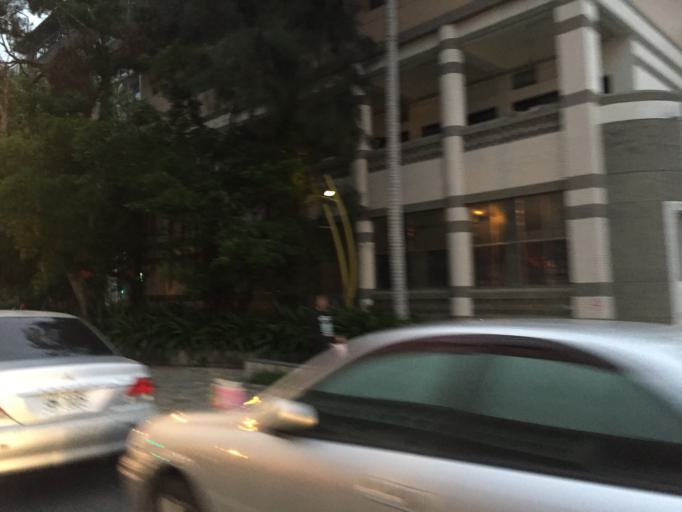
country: TW
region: Taiwan
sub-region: Yilan
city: Yilan
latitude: 24.7544
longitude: 121.7464
